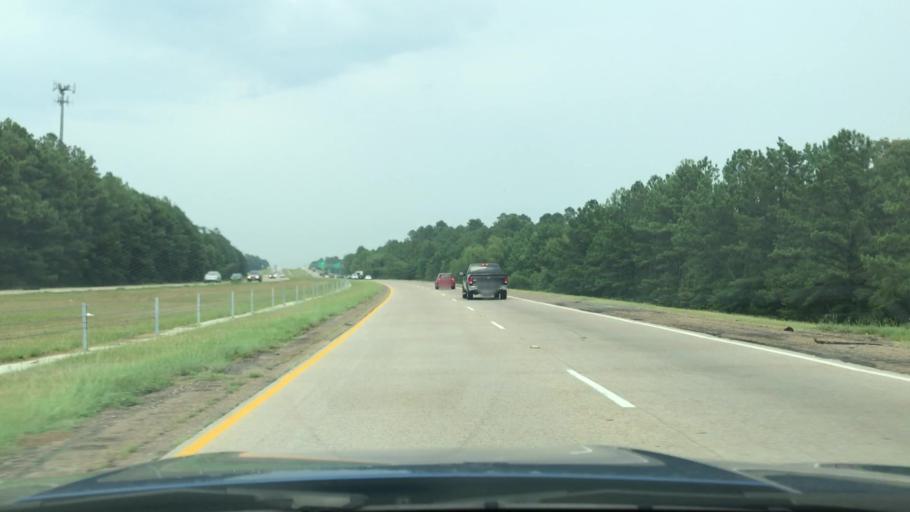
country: US
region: Louisiana
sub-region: Caddo Parish
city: Shreveport
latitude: 32.4174
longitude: -93.8247
